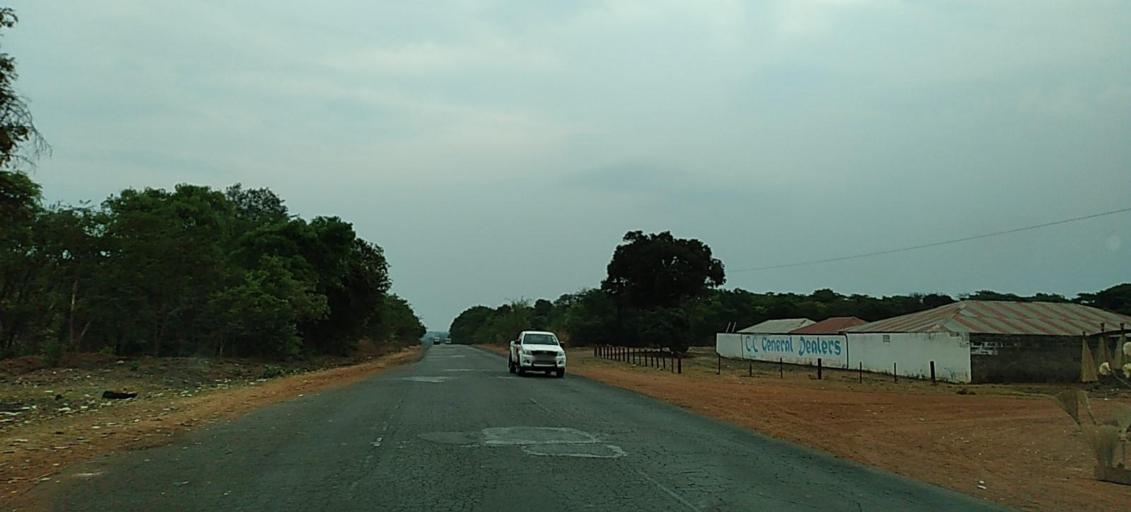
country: ZM
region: Copperbelt
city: Luanshya
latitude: -13.0701
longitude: 28.4512
